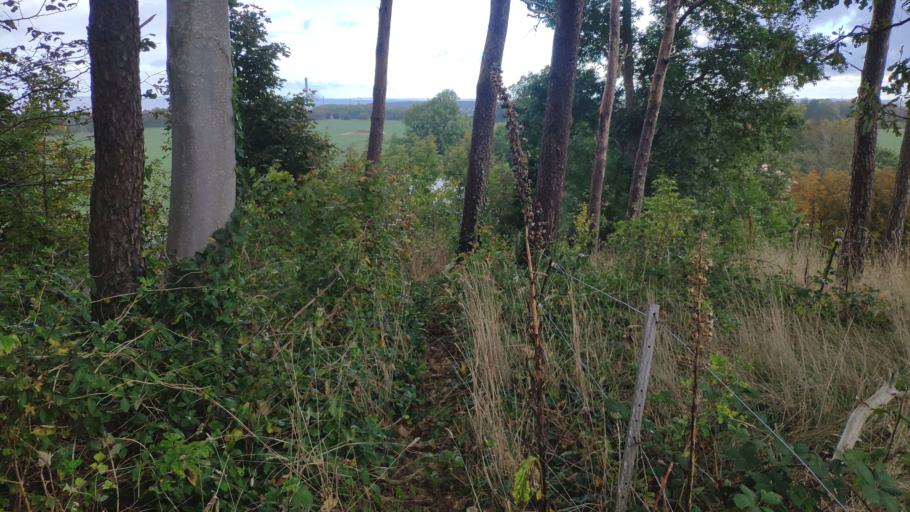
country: DK
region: Capital Region
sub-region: Frederikssund Kommune
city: Skibby
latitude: 55.7861
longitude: 11.8867
